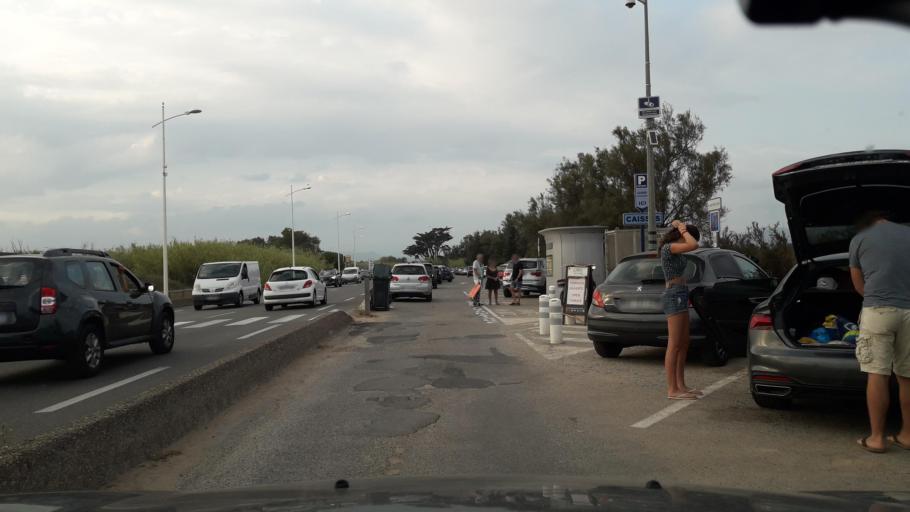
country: FR
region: Provence-Alpes-Cote d'Azur
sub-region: Departement du Var
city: Frejus
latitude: 43.4008
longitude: 6.7300
